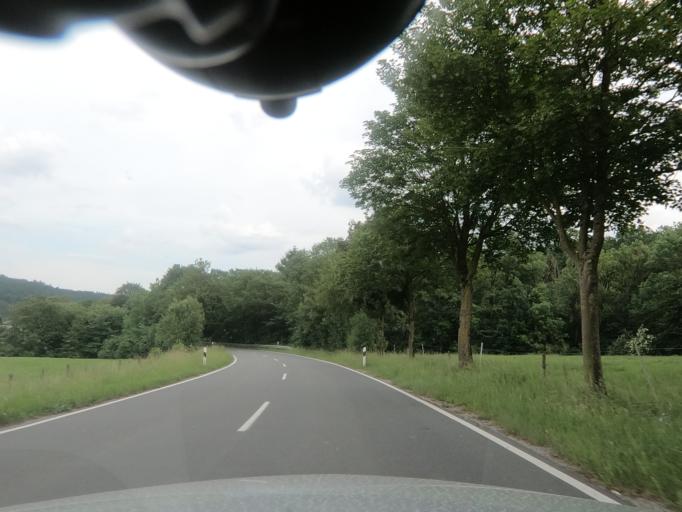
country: DE
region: North Rhine-Westphalia
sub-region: Regierungsbezirk Arnsberg
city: Ruthen
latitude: 51.4414
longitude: 8.4296
